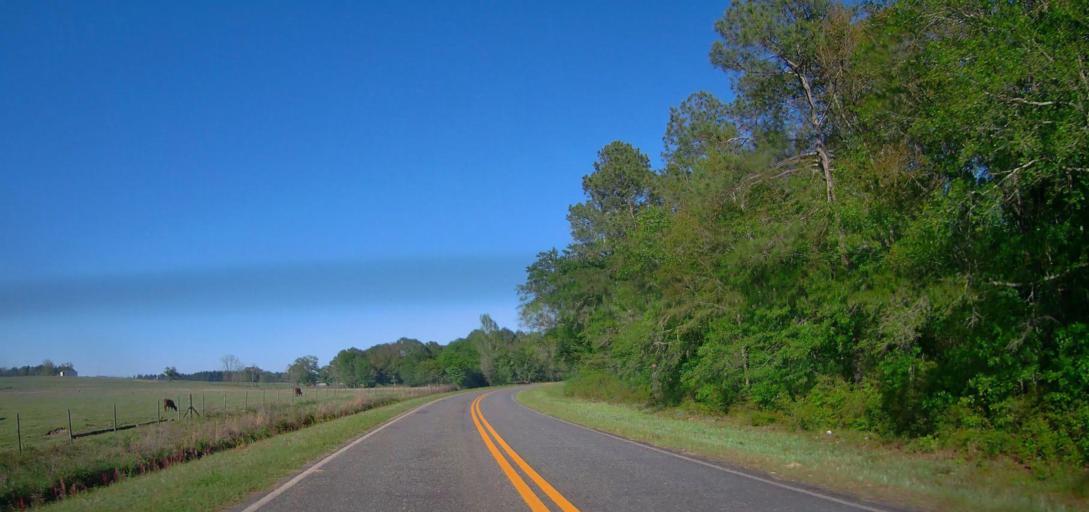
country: US
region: Georgia
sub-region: Turner County
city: Ashburn
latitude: 31.7365
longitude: -83.5041
